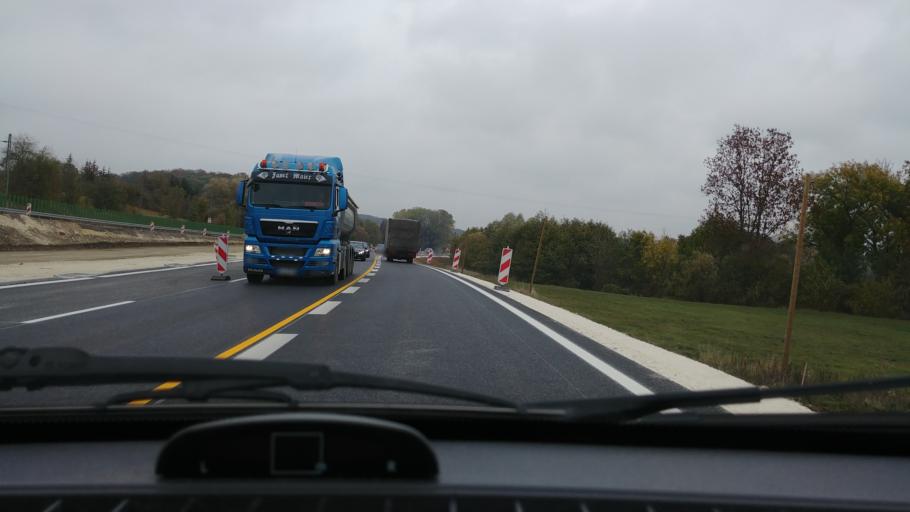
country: DE
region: Baden-Wuerttemberg
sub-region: Regierungsbezirk Stuttgart
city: Mogglingen
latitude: 48.8219
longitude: 9.9947
